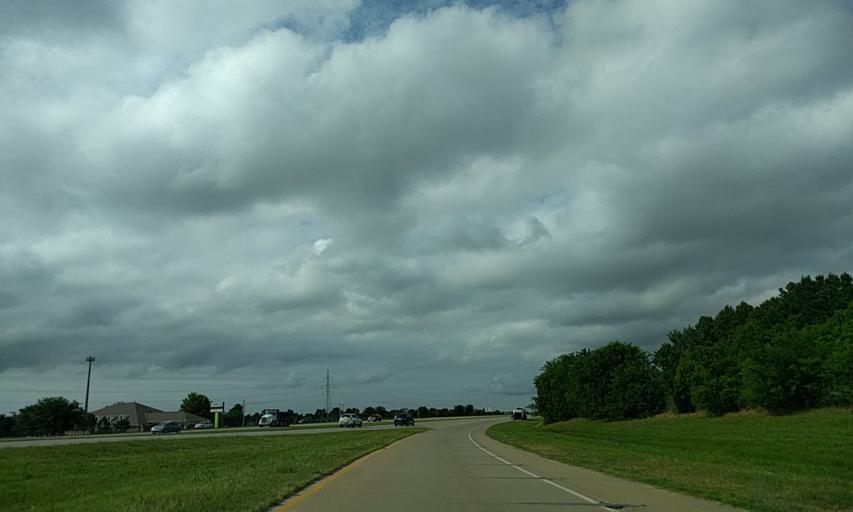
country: US
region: Oklahoma
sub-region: Tulsa County
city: Owasso
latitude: 36.3050
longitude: -95.8229
